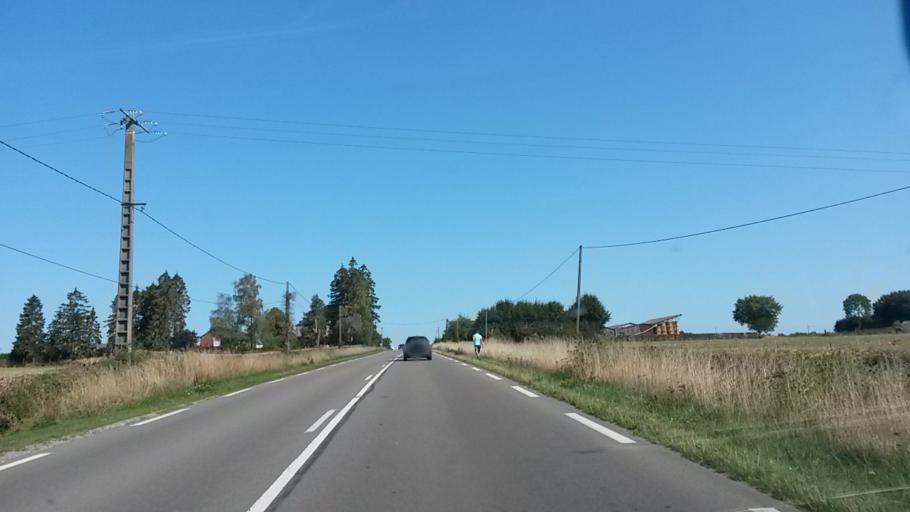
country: FR
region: Nord-Pas-de-Calais
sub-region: Departement du Nord
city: Avesnes-sur-Helpe
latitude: 50.0915
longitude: 3.9303
